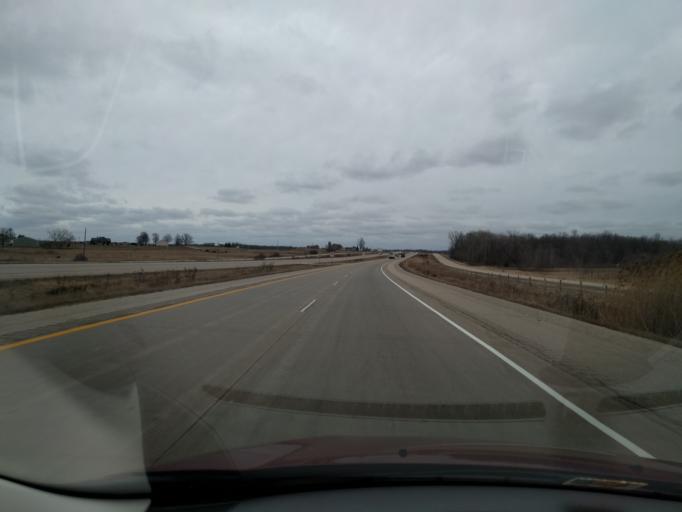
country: US
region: Wisconsin
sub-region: Winnebago County
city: Winneconne
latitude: 44.2318
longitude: -88.7210
